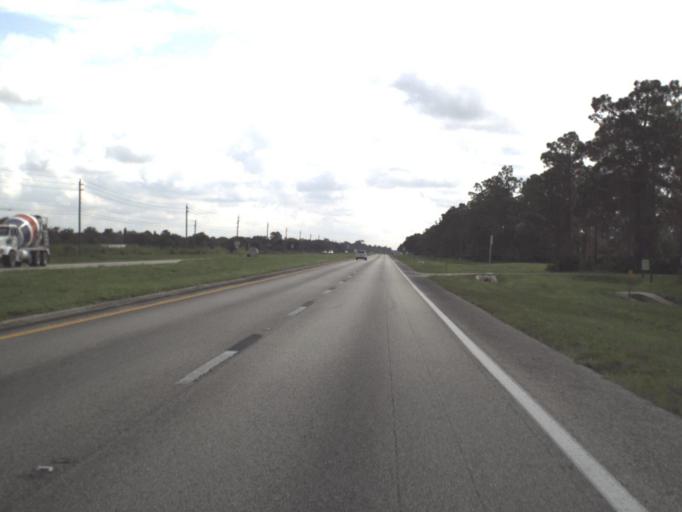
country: US
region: Florida
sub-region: Lee County
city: Olga
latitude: 26.7139
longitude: -81.6652
